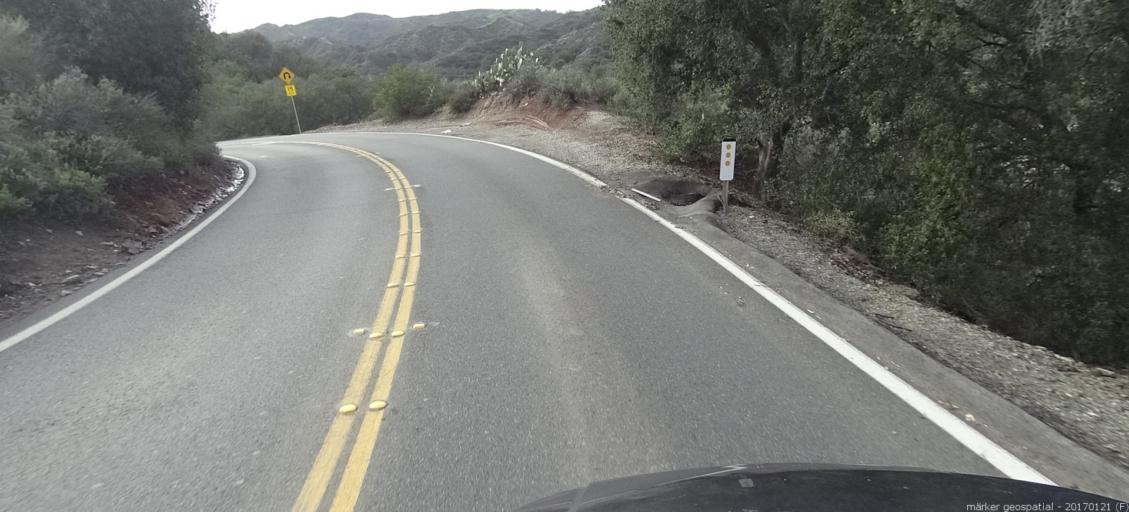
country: US
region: California
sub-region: Orange County
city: Trabuco Canyon
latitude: 33.6580
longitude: -117.5849
